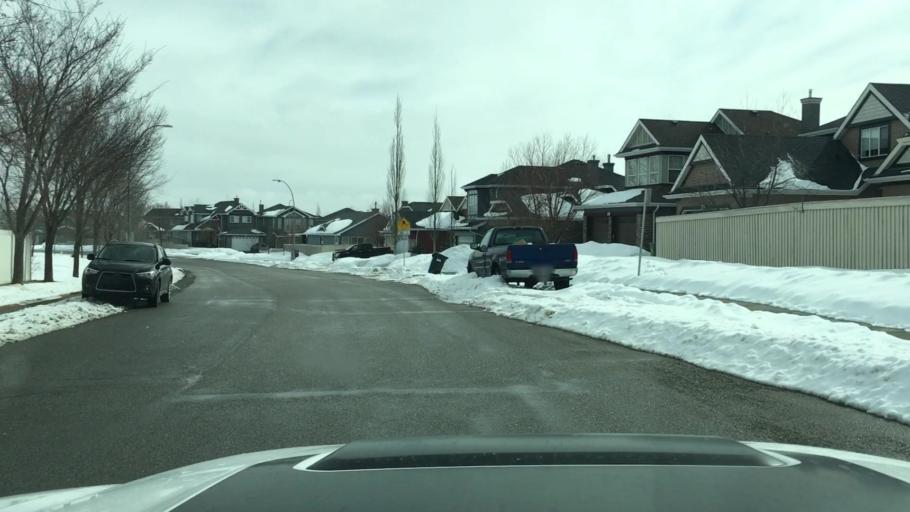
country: CA
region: Alberta
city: Calgary
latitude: 51.1477
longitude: -114.2310
